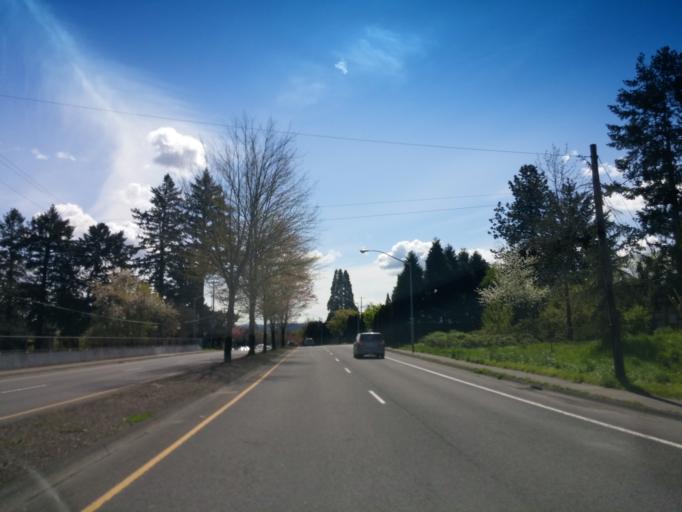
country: US
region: Oregon
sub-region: Washington County
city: Cedar Mill
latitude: 45.5184
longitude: -122.8168
